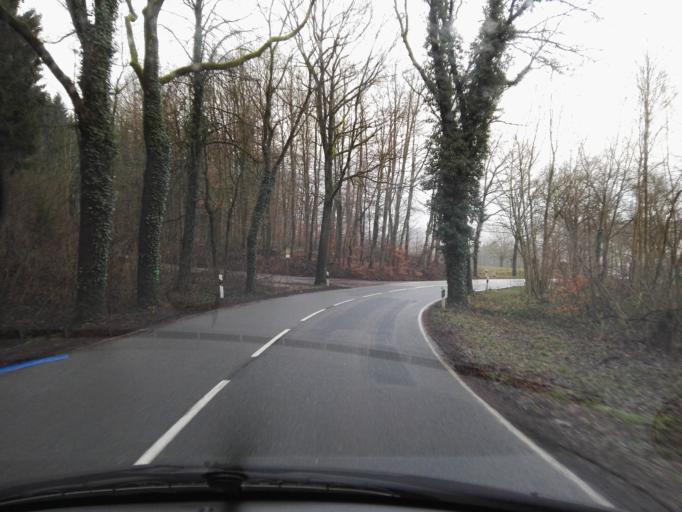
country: DE
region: Lower Saxony
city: Diekholzen
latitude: 52.0823
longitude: 9.9081
